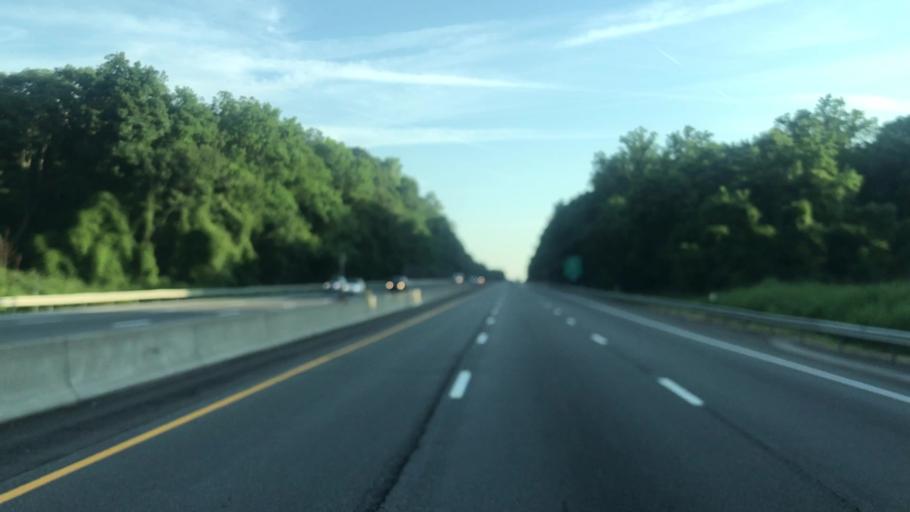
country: US
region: New York
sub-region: Westchester County
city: Ardsley
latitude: 40.9901
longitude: -73.8532
